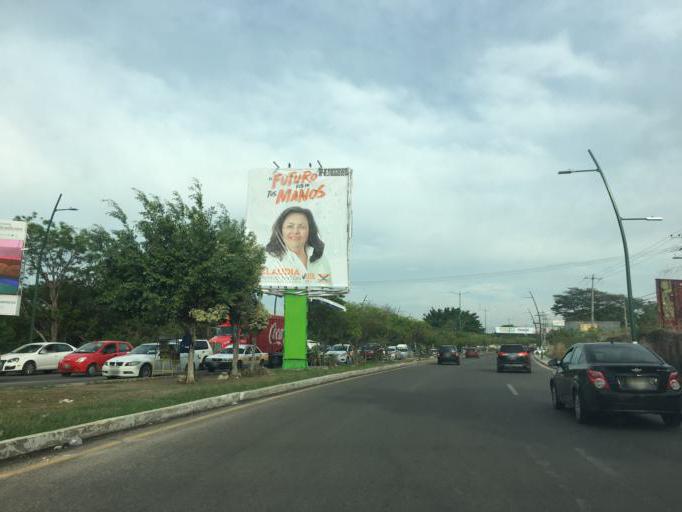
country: MX
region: Chiapas
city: Tuxtla Gutierrez
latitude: 16.7608
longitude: -93.1465
